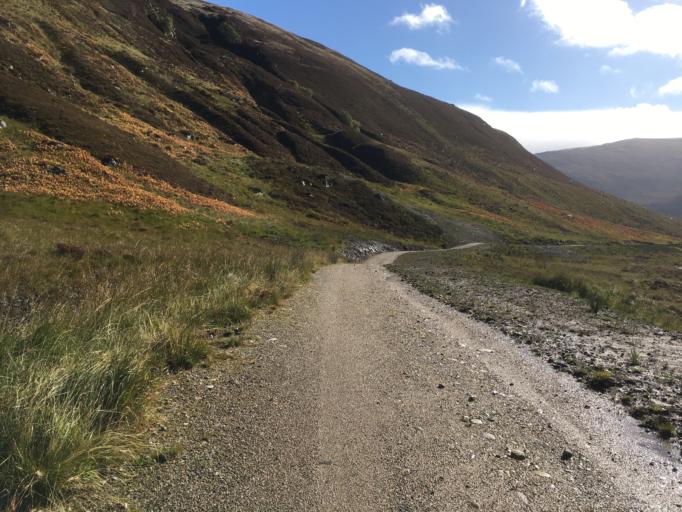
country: GB
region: Scotland
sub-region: Highland
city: Spean Bridge
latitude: 57.3508
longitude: -4.9845
